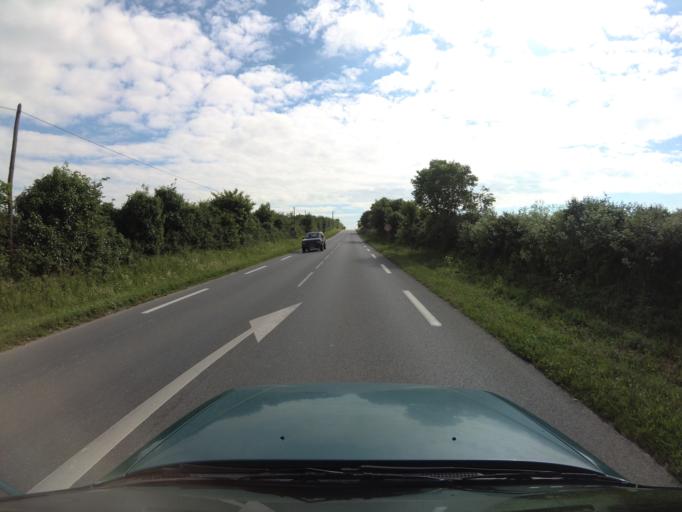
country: FR
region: Poitou-Charentes
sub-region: Departement de la Charente-Maritime
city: Saint-Xandre
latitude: 46.2284
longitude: -1.0800
